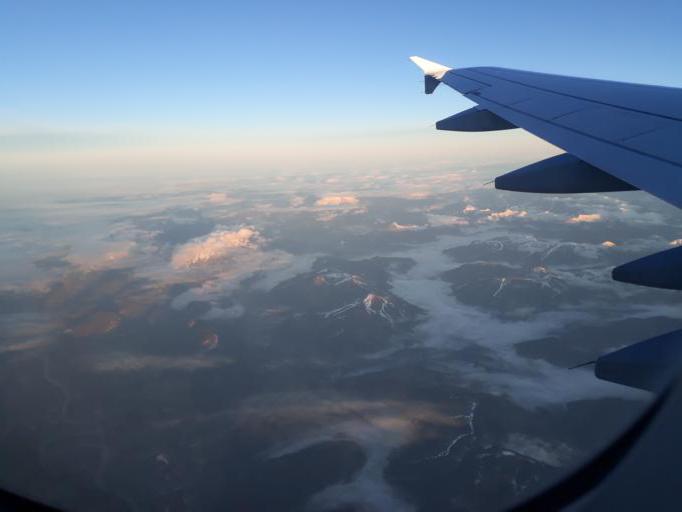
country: AT
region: Tyrol
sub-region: Politischer Bezirk Kufstein
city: Radfeld
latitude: 47.4330
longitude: 11.9383
